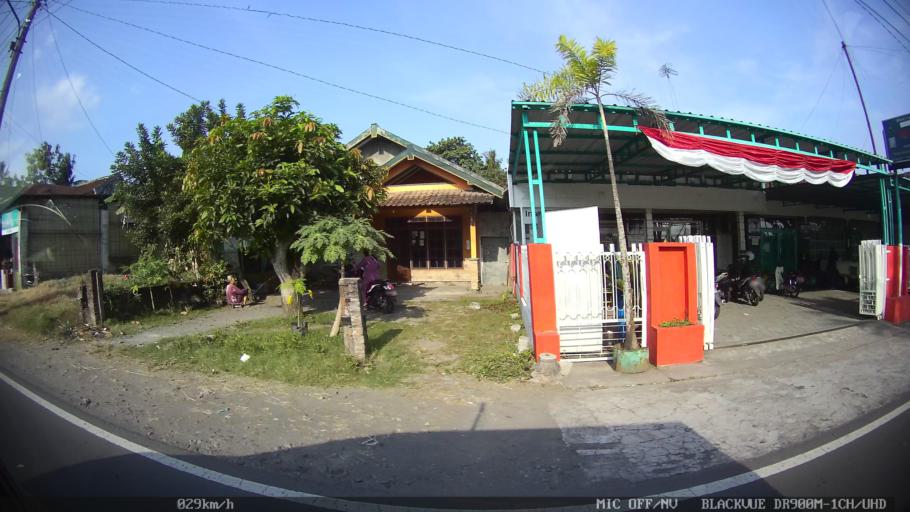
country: ID
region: Daerah Istimewa Yogyakarta
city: Bantul
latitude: -7.8882
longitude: 110.3176
